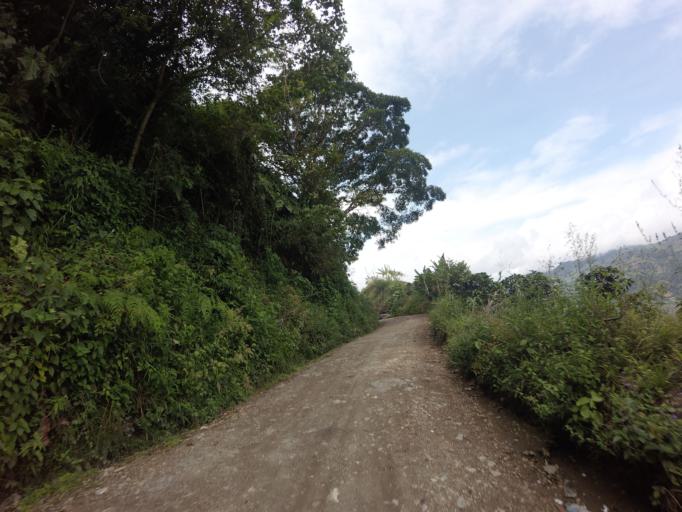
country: CO
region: Caldas
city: Marquetalia
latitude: 5.3533
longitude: -75.0573
